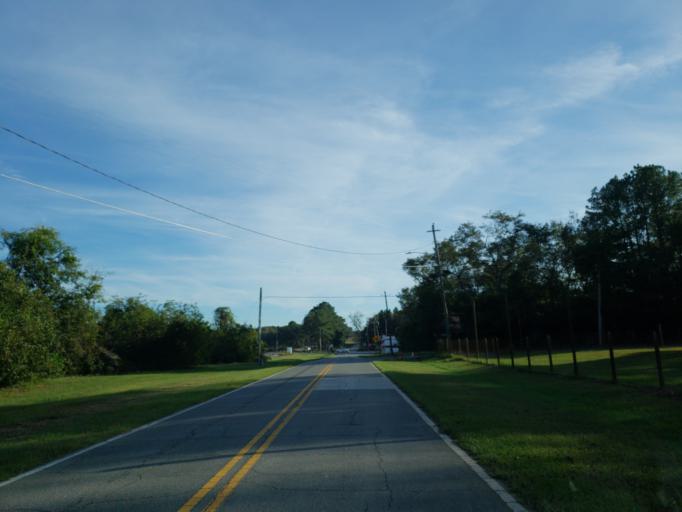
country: US
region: Georgia
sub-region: Dooly County
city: Vienna
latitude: 32.0924
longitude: -83.7876
